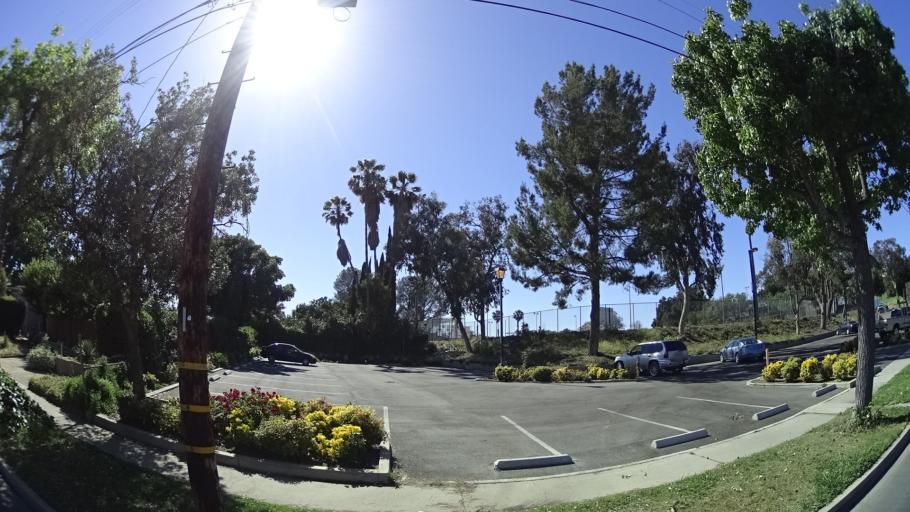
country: US
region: California
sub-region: Los Angeles County
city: Monterey Park
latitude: 34.0662
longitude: -118.1448
